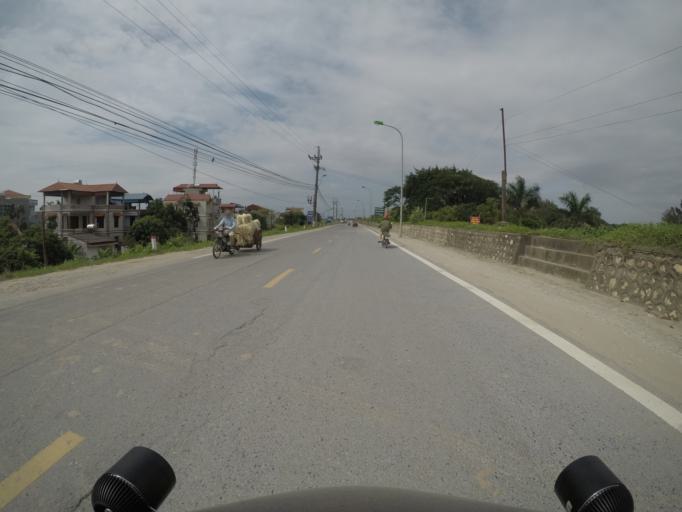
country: VN
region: Ha Noi
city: Cau Dien
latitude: 21.0889
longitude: 105.7596
